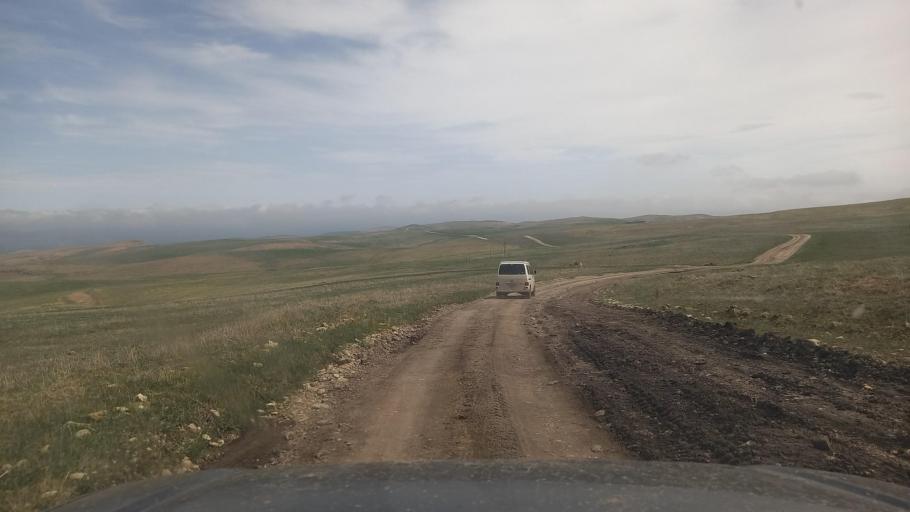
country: RU
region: Stavropol'skiy
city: Kislovodsk
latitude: 43.7594
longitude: 42.7822
